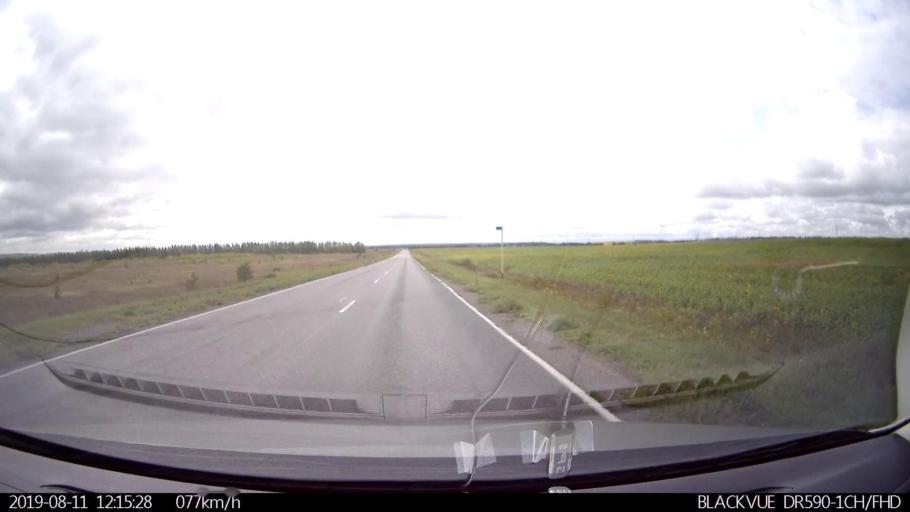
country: RU
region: Ulyanovsk
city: Ignatovka
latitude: 53.9414
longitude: 47.9683
